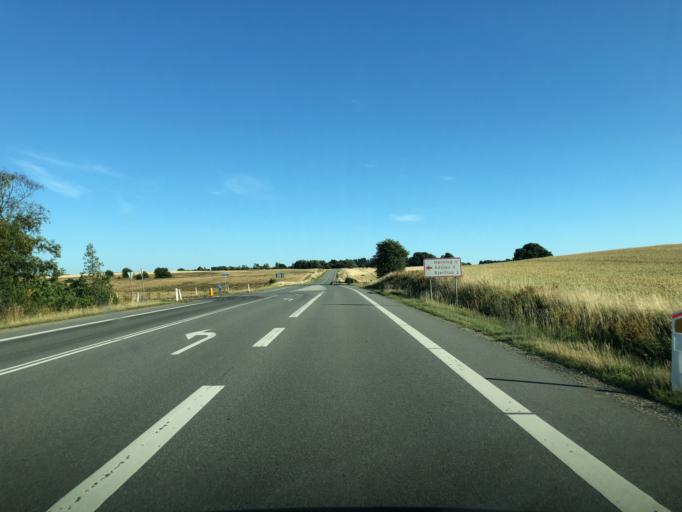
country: DK
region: Central Jutland
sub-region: Skanderborg Kommune
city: Stilling
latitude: 56.0901
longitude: 9.9701
